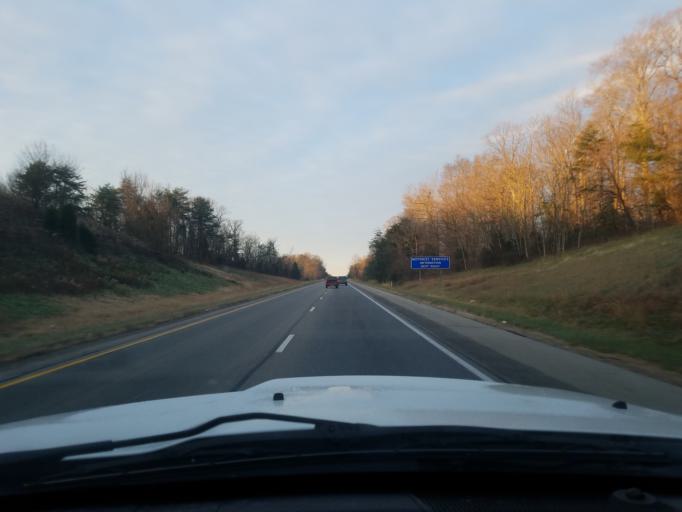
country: US
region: Indiana
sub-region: Floyd County
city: Georgetown
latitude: 38.2816
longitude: -85.9462
